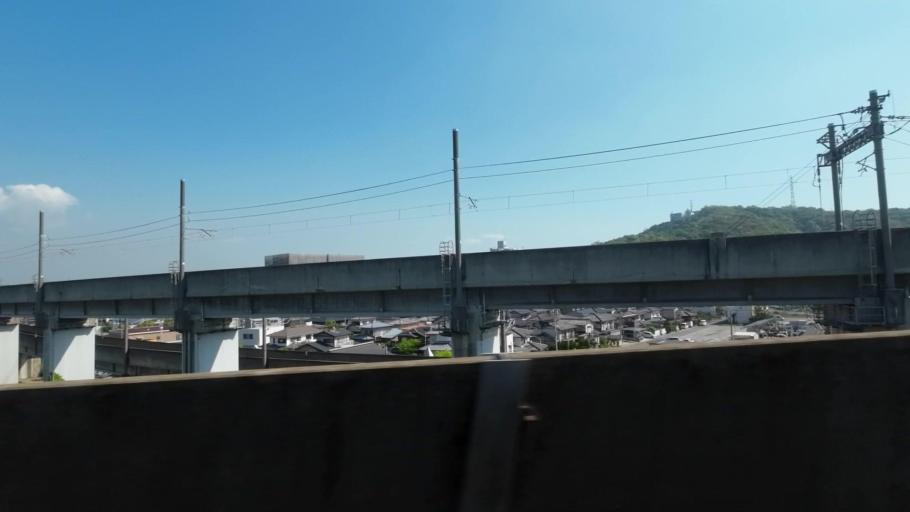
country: JP
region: Kagawa
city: Sakaidecho
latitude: 34.3140
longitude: 133.8240
